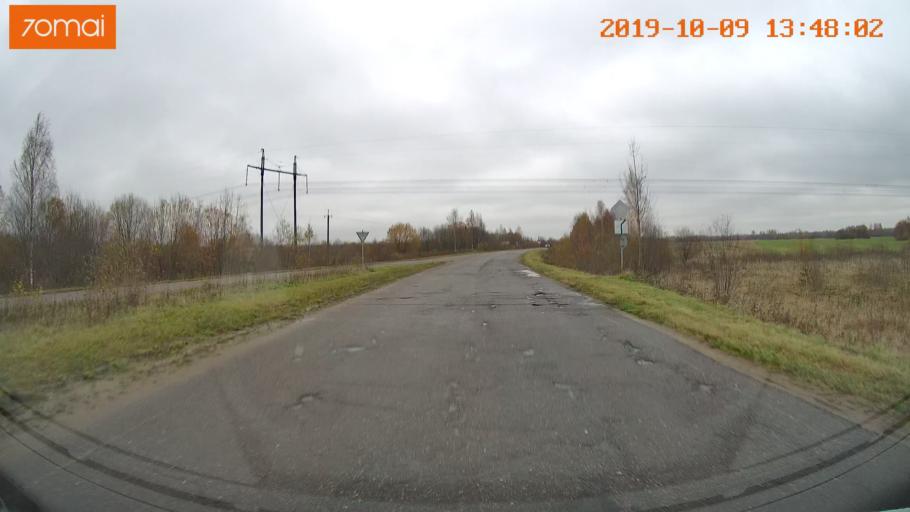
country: RU
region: Kostroma
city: Buy
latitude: 58.3976
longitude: 41.2281
